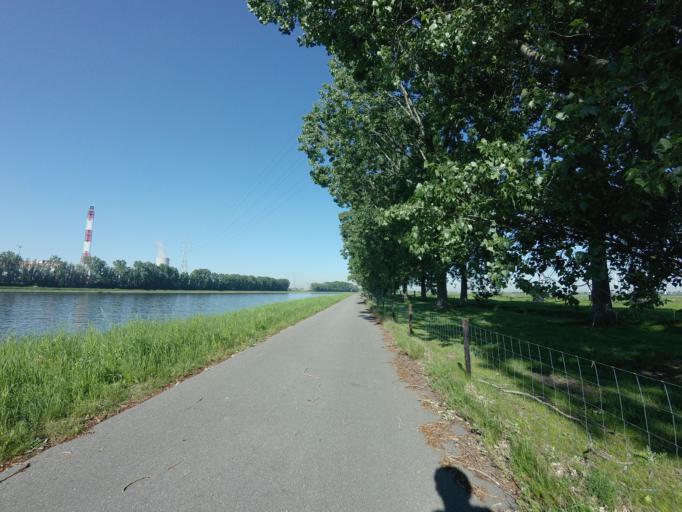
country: NL
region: North Brabant
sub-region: Gemeente Woensdrecht
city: Woensdrecht
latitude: 51.3750
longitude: 4.2783
